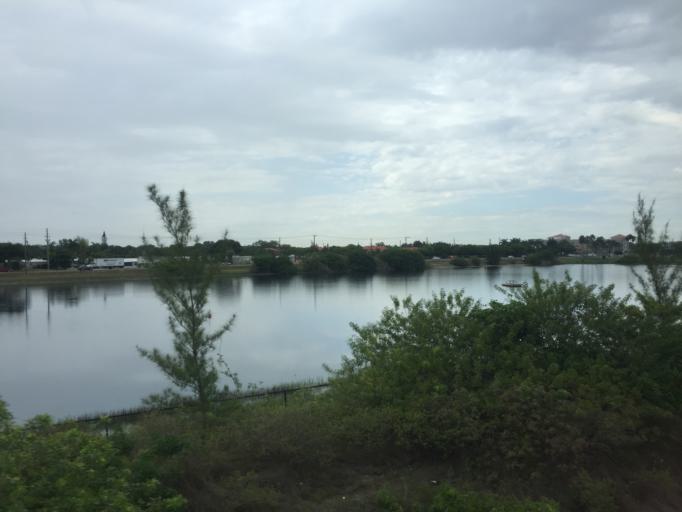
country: US
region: Florida
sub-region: Broward County
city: Dania Beach
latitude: 26.0571
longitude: -80.1664
